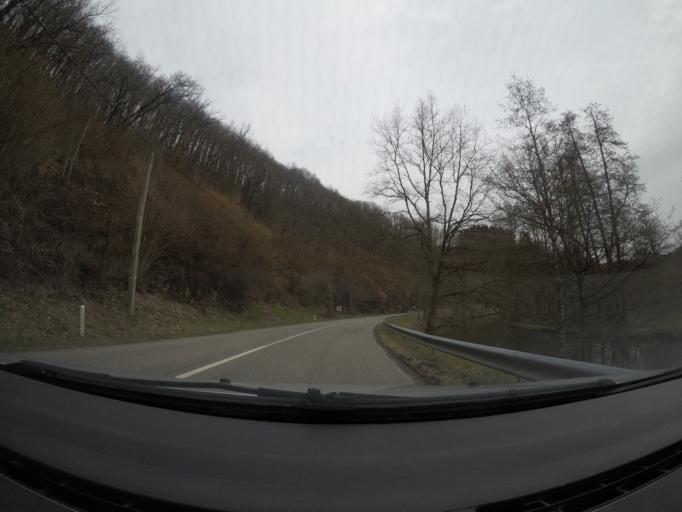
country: BE
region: Wallonia
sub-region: Province du Luxembourg
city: Martelange
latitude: 49.8357
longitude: 5.7295
